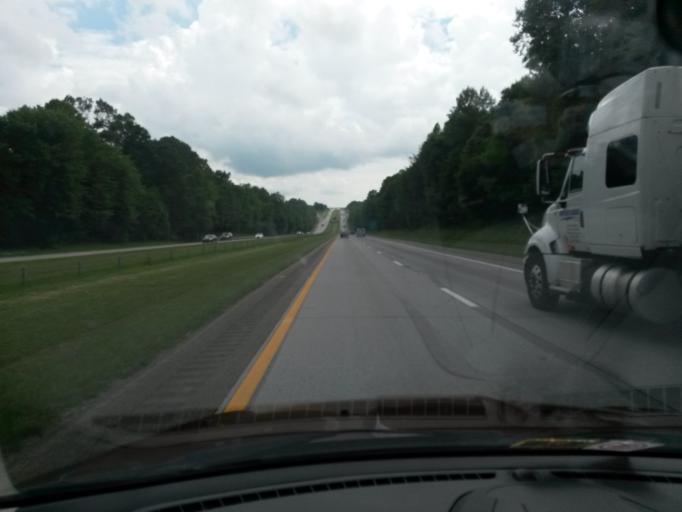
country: US
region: North Carolina
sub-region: Surry County
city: Elkin
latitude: 36.2937
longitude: -80.8141
